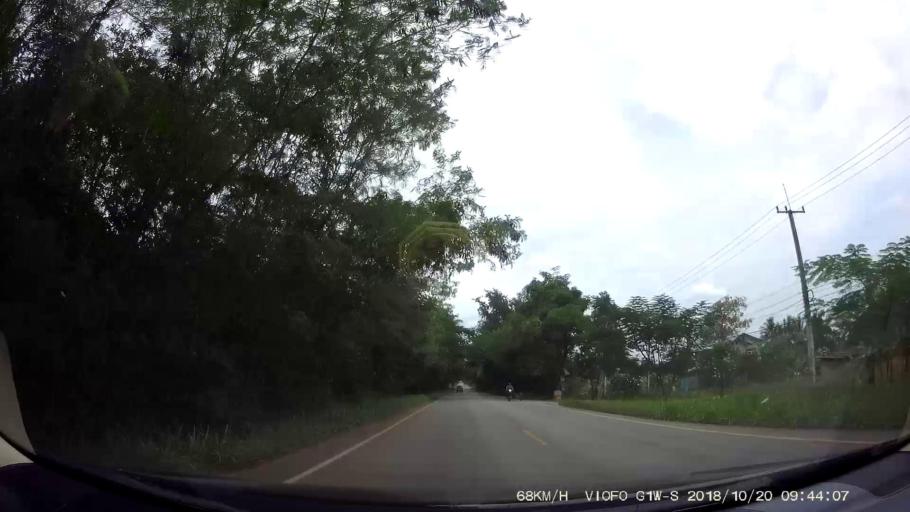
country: TH
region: Chaiyaphum
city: Khon San
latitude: 16.4799
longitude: 101.9453
